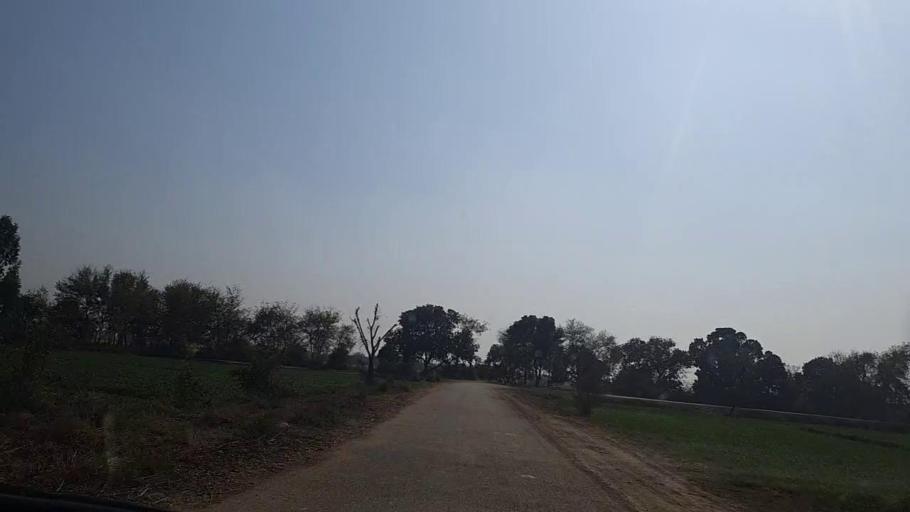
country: PK
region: Sindh
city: Sakrand
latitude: 26.0302
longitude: 68.4070
